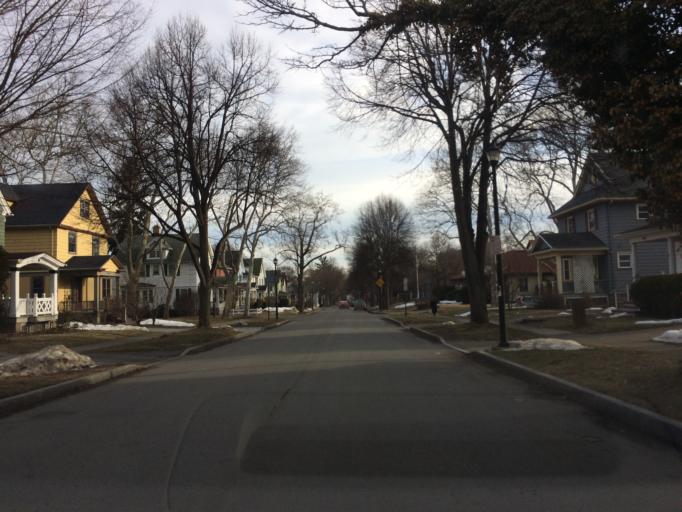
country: US
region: New York
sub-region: Monroe County
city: Rochester
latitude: 43.1361
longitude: -77.6015
